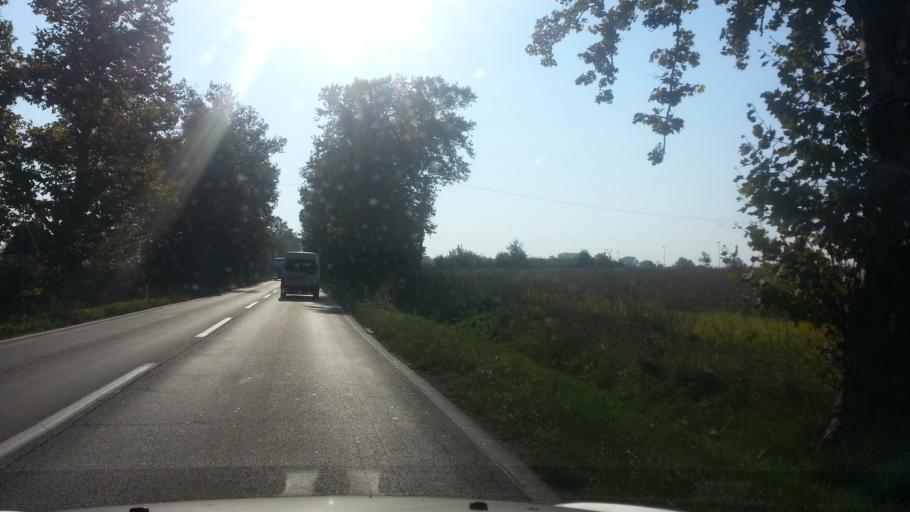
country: RS
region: Central Serbia
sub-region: Belgrade
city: Zemun
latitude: 44.8775
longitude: 20.3354
